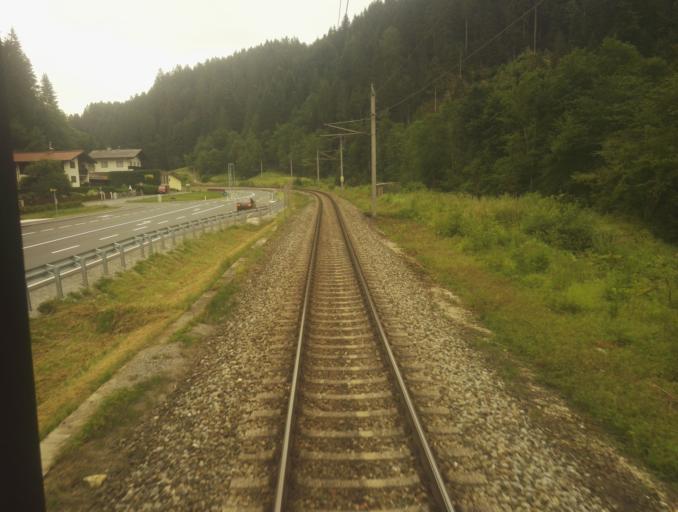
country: AT
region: Salzburg
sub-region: Politischer Bezirk Sankt Johann im Pongau
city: Bischofshofen
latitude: 47.4315
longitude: 13.2411
